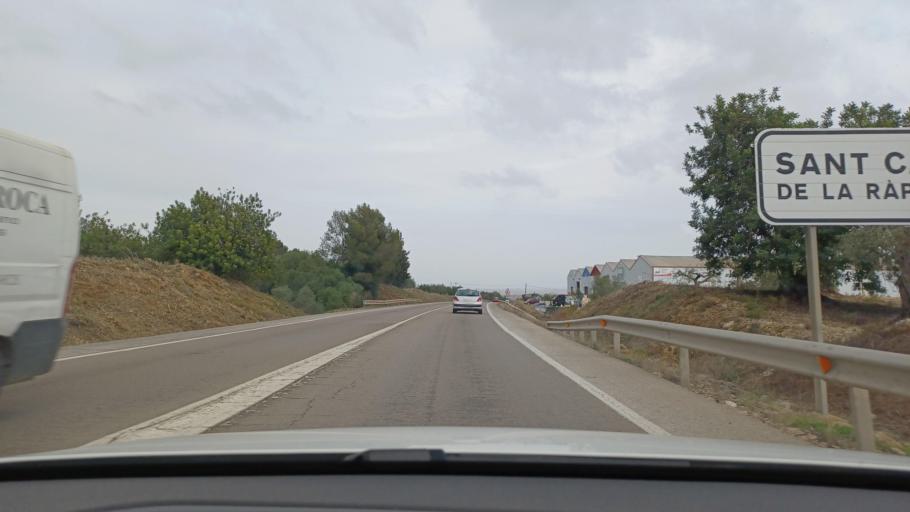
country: ES
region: Catalonia
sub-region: Provincia de Tarragona
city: Sant Carles de la Rapita
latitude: 40.6285
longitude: 0.5806
